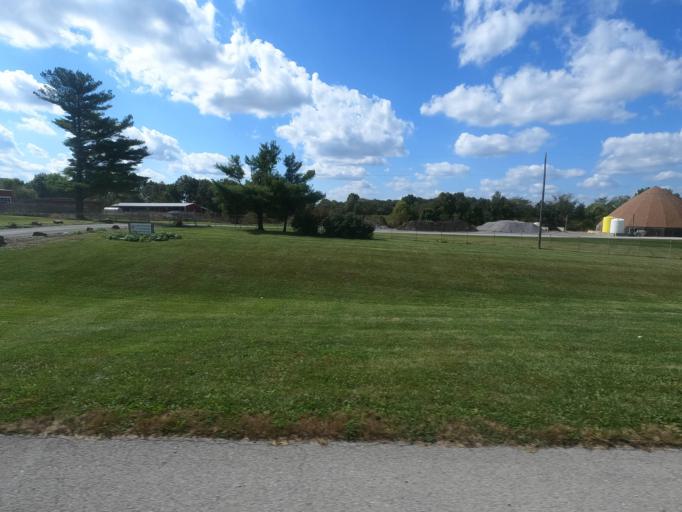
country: US
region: Illinois
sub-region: Johnson County
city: Vienna
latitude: 37.4342
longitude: -88.8929
